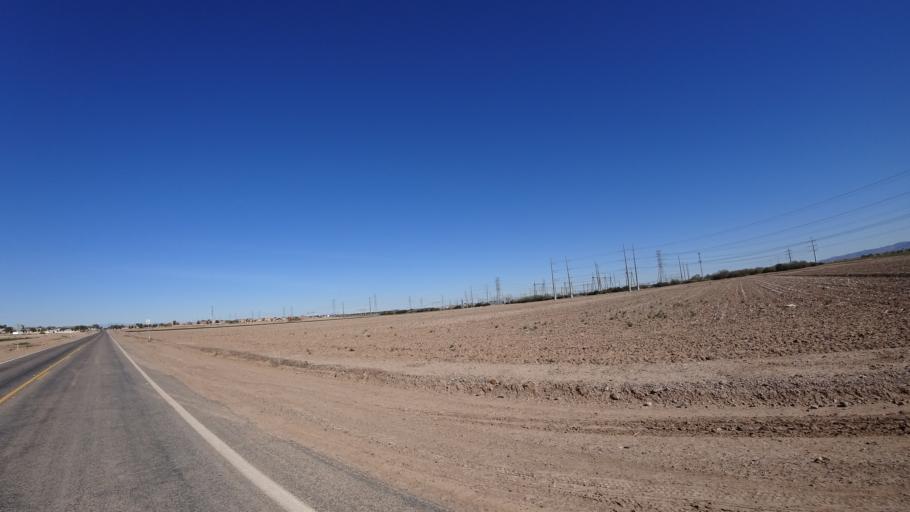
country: US
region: Arizona
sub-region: Maricopa County
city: Avondale
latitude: 33.4069
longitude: -112.3233
